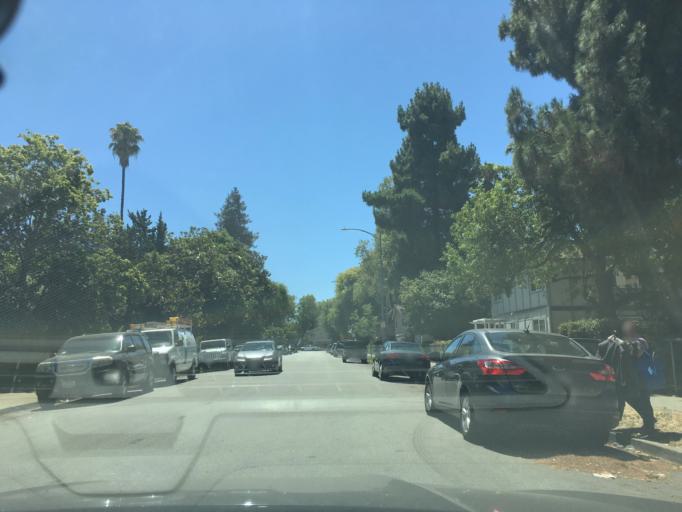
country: US
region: California
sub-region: Santa Clara County
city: Cambrian Park
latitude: 37.2468
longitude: -121.8776
